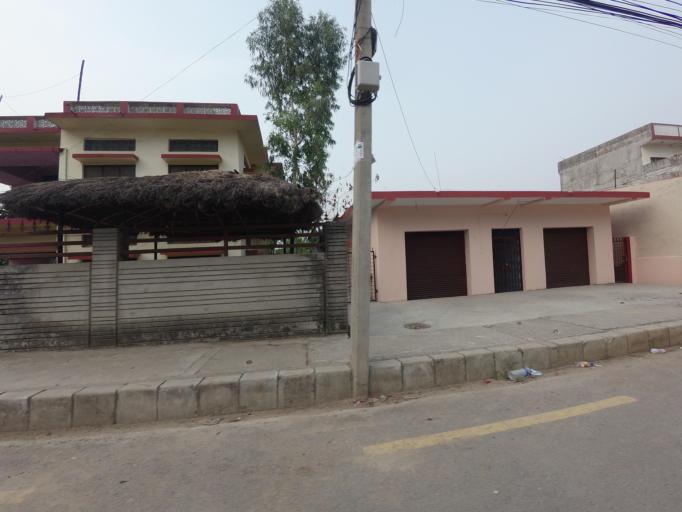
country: NP
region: Western Region
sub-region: Lumbini Zone
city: Bhairahawa
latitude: 27.5193
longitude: 83.4454
